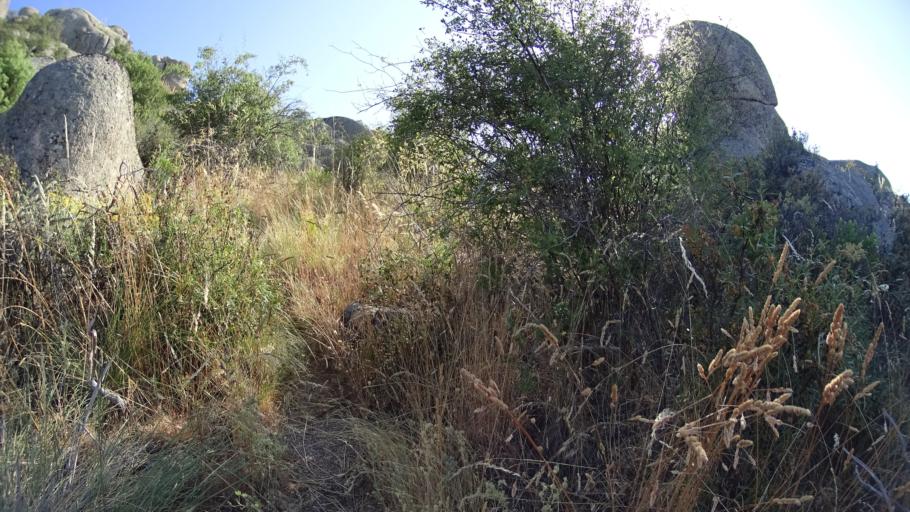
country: ES
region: Madrid
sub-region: Provincia de Madrid
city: Moralzarzal
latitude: 40.6504
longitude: -3.9489
